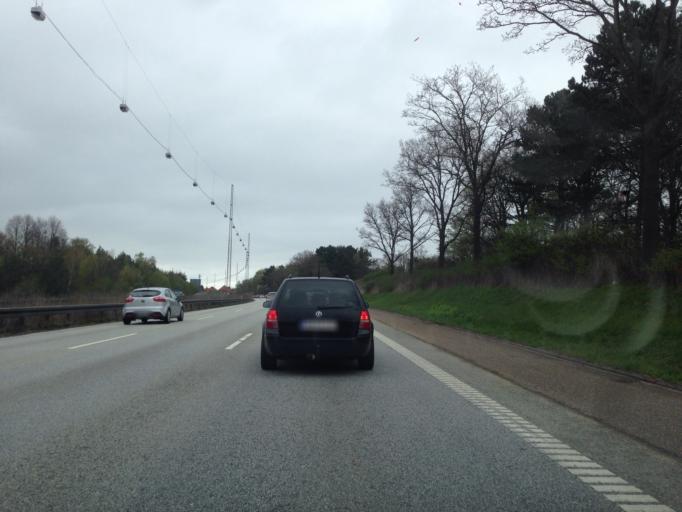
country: DK
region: Capital Region
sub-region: Rudersdal Kommune
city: Trorod
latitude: 55.8050
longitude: 12.5333
